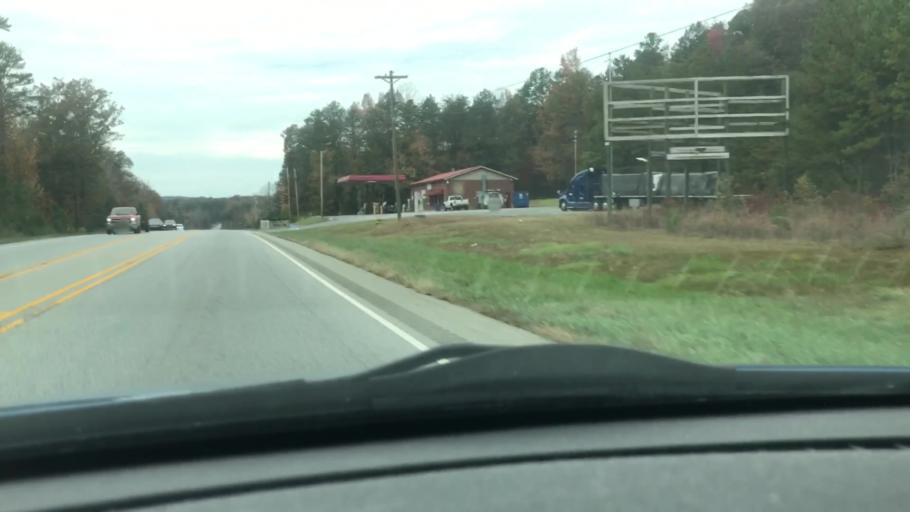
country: US
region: North Carolina
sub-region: Randolph County
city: Trinity
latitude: 35.7351
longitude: -79.9747
